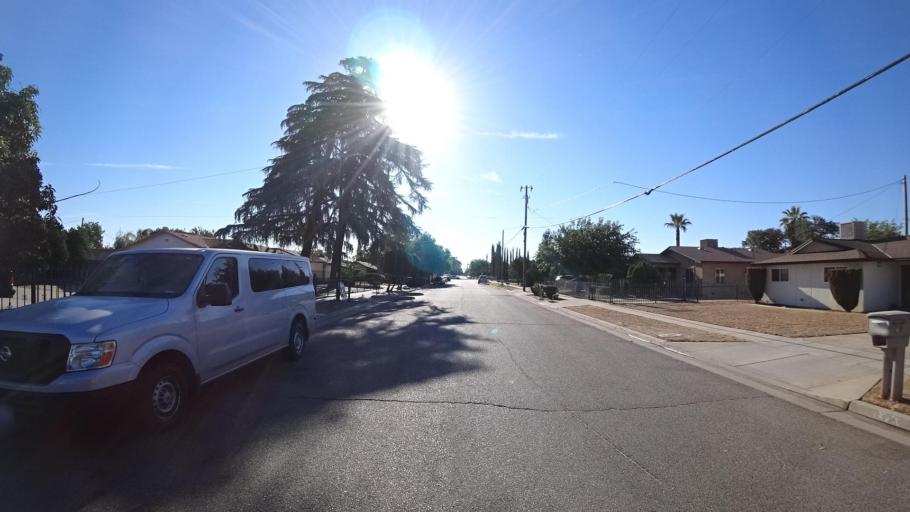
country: US
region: California
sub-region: Fresno County
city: Fresno
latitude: 36.7522
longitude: -119.7379
